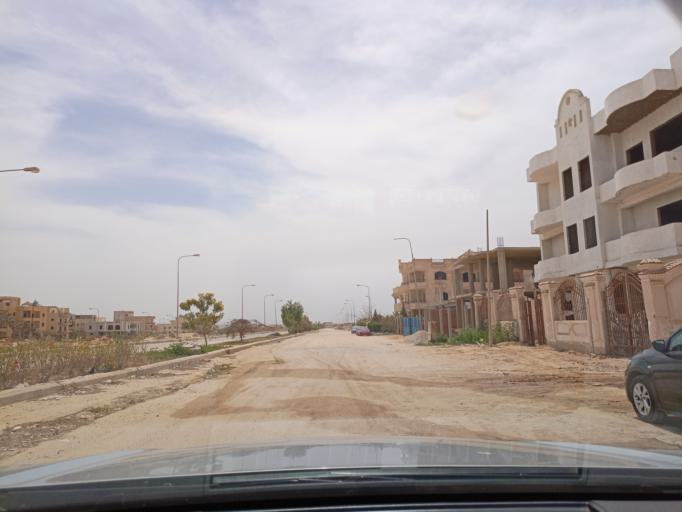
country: EG
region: Muhafazat al Qalyubiyah
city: Al Khankah
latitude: 30.2353
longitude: 31.4883
